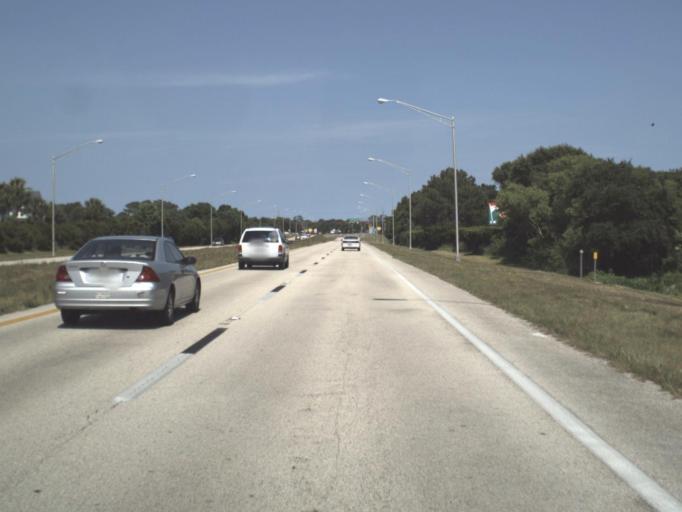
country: US
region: Florida
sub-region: Saint Johns County
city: Saint Augustine Beach
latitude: 29.8614
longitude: -81.2874
